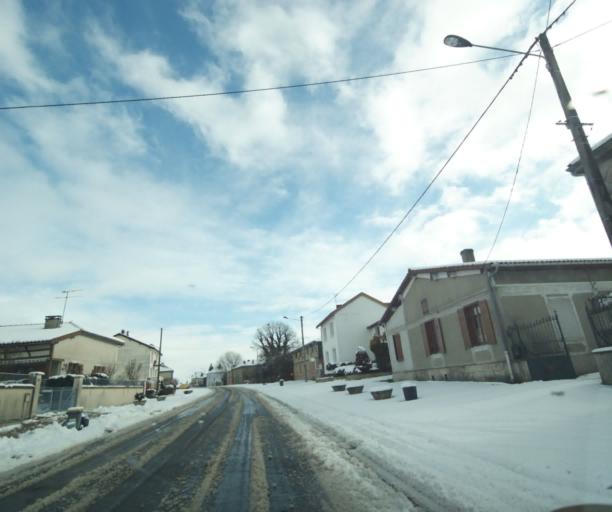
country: FR
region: Champagne-Ardenne
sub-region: Departement de la Haute-Marne
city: Montier-en-Der
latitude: 48.4545
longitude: 4.6848
